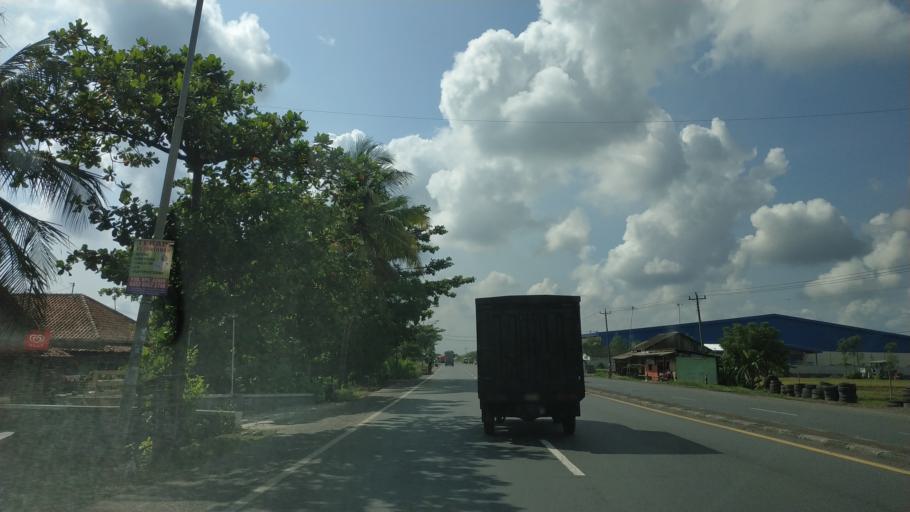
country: ID
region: Central Java
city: Comal
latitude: -6.8872
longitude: 109.5745
